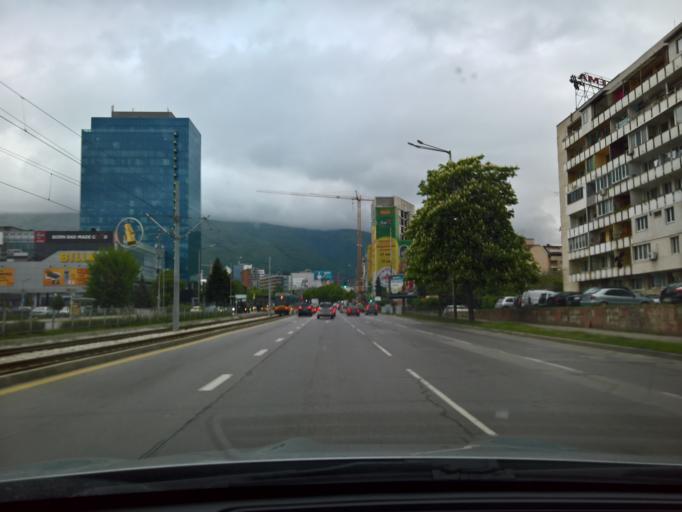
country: BG
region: Sofia-Capital
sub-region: Stolichna Obshtina
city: Sofia
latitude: 42.6659
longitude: 23.2882
